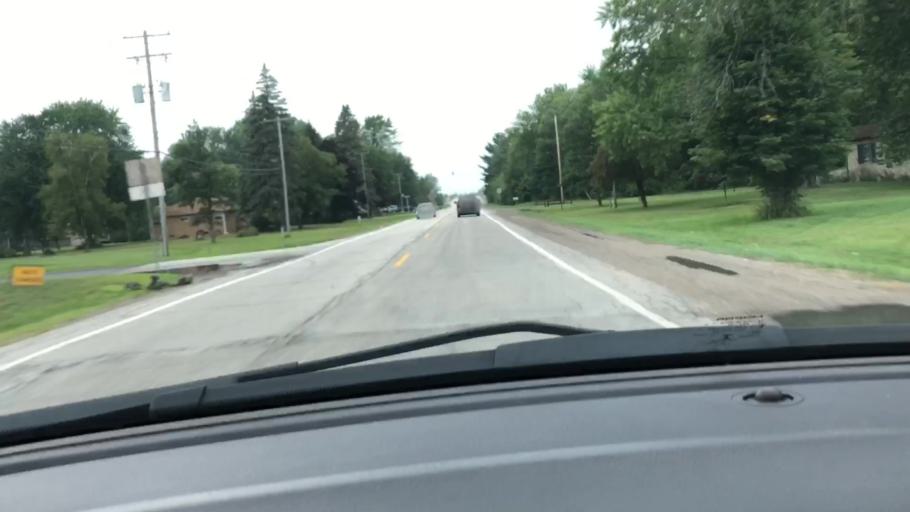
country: US
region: Michigan
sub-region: Bay County
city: Auburn
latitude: 43.6046
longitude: -84.1487
